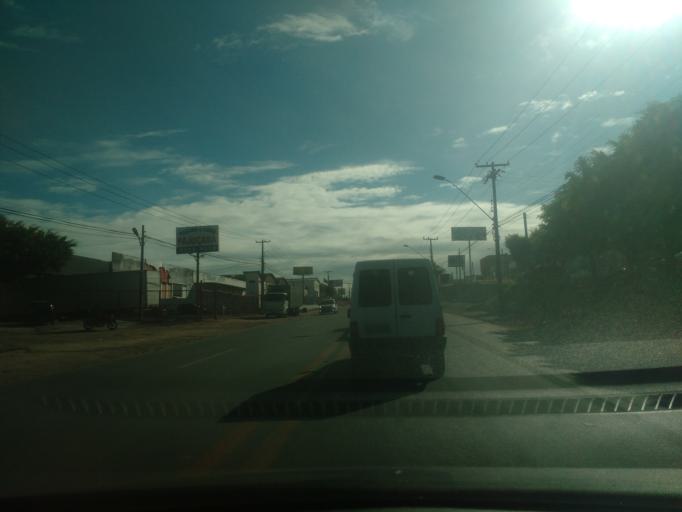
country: BR
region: Alagoas
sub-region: Satuba
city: Satuba
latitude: -9.5631
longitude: -35.7715
